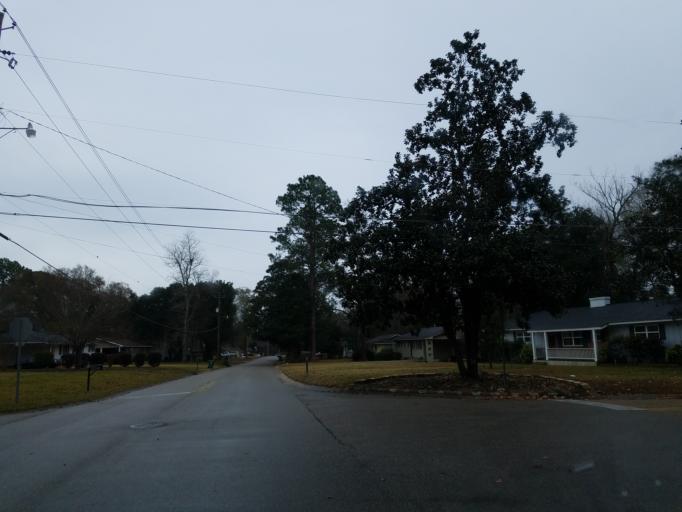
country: US
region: Mississippi
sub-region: Lamar County
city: West Hattiesburg
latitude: 31.3111
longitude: -89.3341
